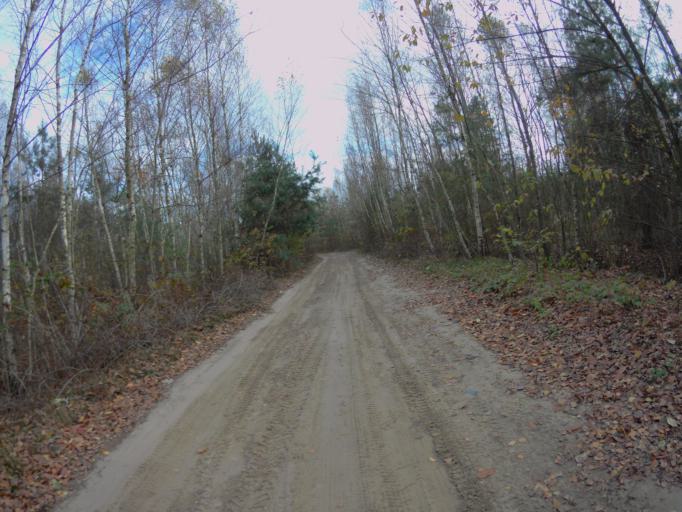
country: PL
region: Subcarpathian Voivodeship
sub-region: Powiat kolbuszowski
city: Lipnica
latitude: 50.3251
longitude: 21.9390
